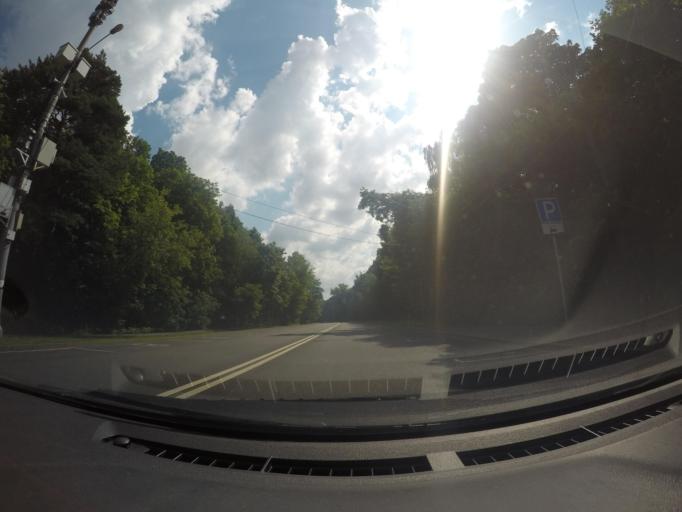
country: RU
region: Moscow
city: Sokol'niki
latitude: 55.8109
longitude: 37.6849
